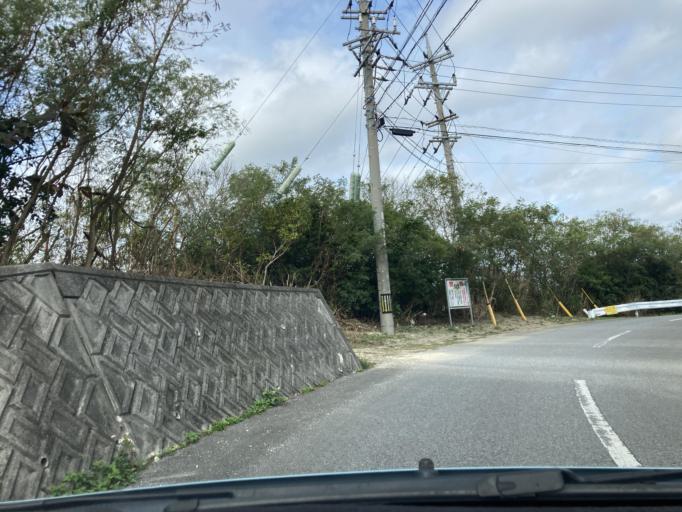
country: JP
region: Okinawa
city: Ginowan
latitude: 26.2079
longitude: 127.7447
